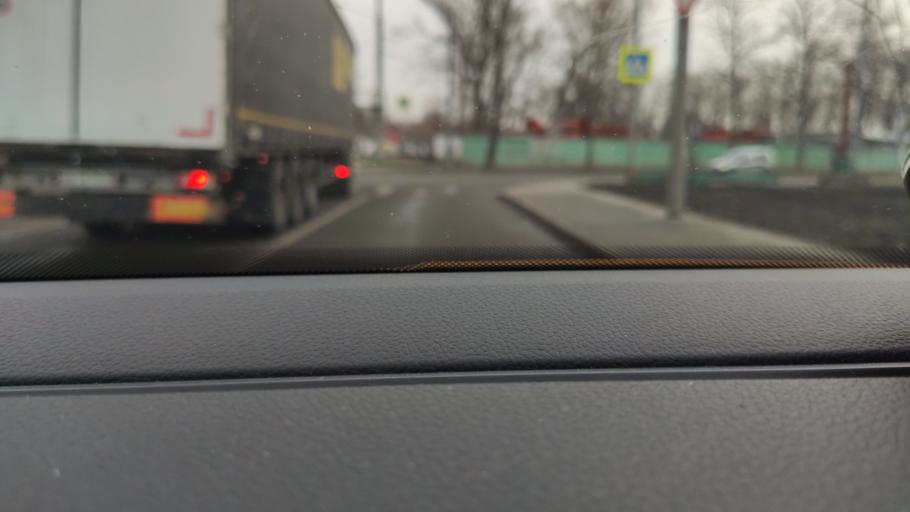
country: RU
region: Moscow
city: Vagonoremont
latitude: 55.8990
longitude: 37.5300
